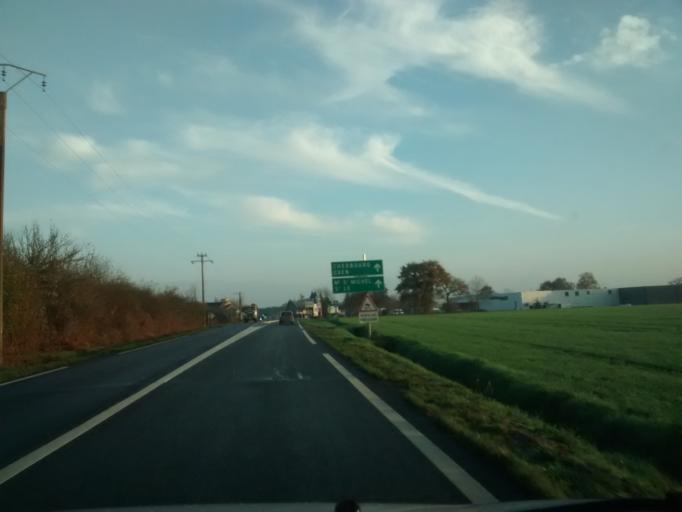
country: FR
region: Brittany
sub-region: Departement d'Ille-et-Vilaine
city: Sens-de-Bretagne
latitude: 48.3282
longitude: -1.5267
